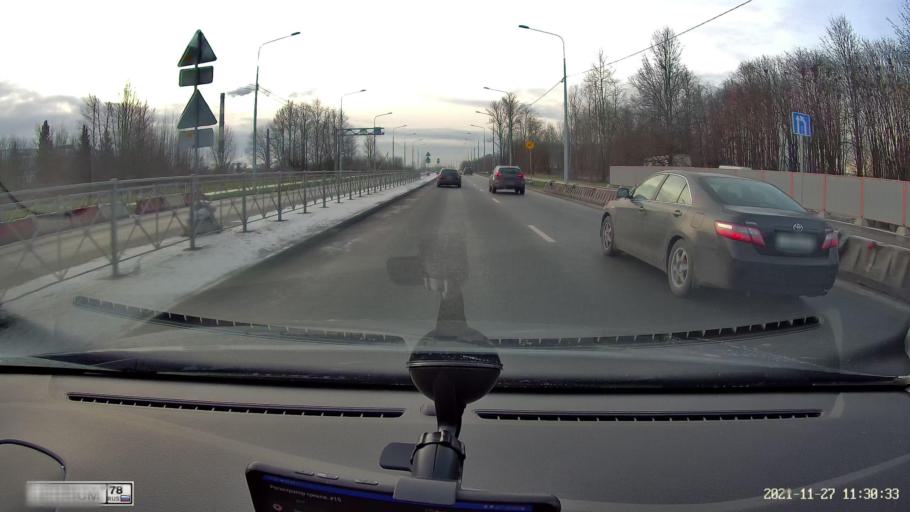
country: RU
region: St.-Petersburg
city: Krasnoye Selo
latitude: 59.7292
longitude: 30.0563
